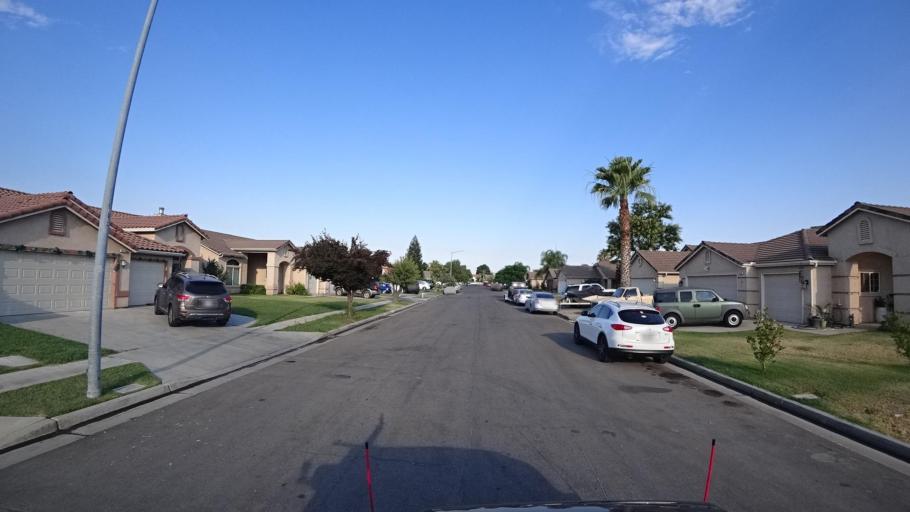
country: US
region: California
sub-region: Fresno County
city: Sunnyside
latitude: 36.7107
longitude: -119.7041
